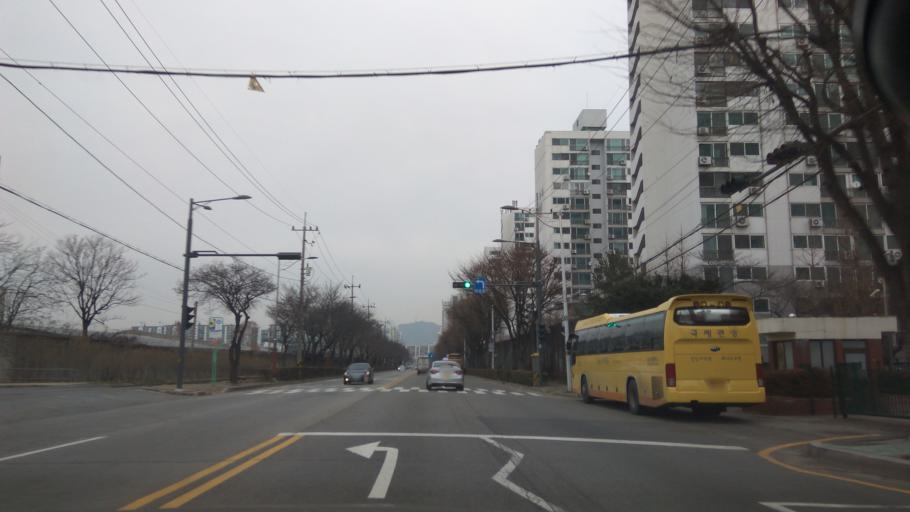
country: KR
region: Incheon
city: Incheon
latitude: 37.4934
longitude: 126.7165
